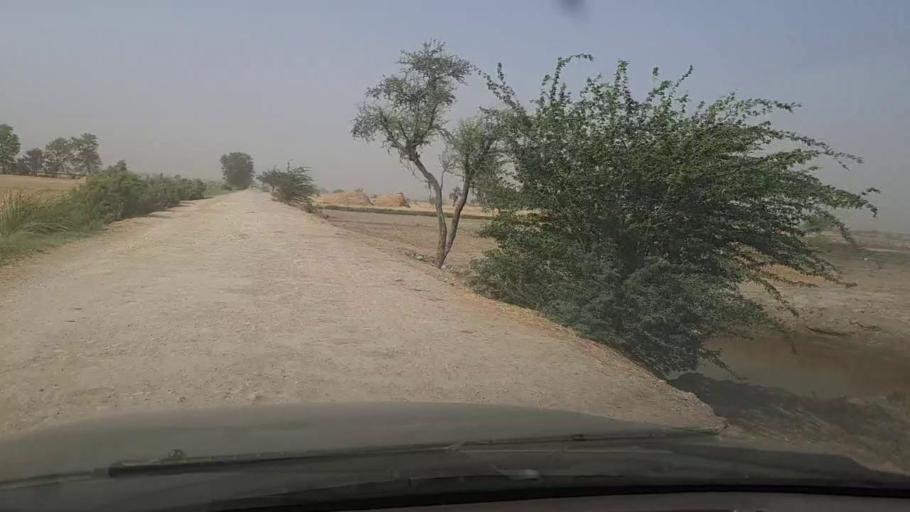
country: PK
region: Sindh
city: Garhi Yasin
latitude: 27.8956
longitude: 68.5856
